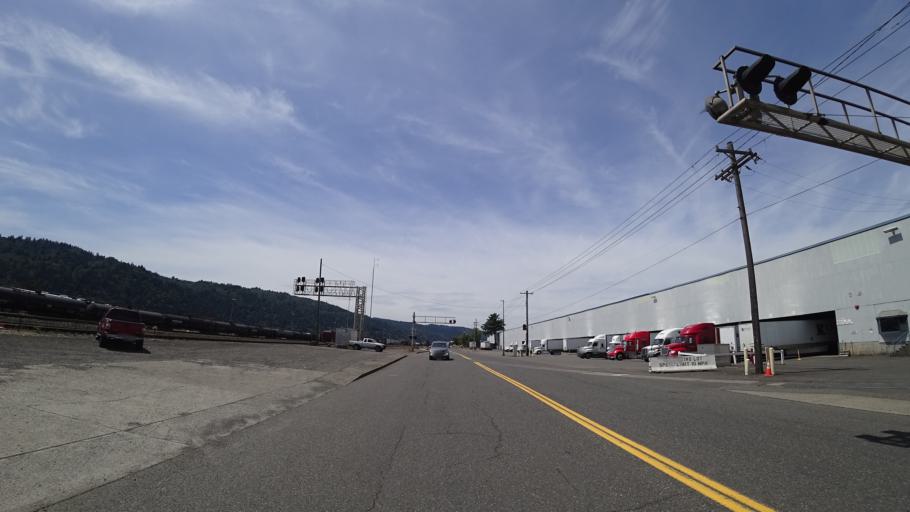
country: US
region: Oregon
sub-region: Multnomah County
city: Portland
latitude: 45.5499
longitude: -122.7093
